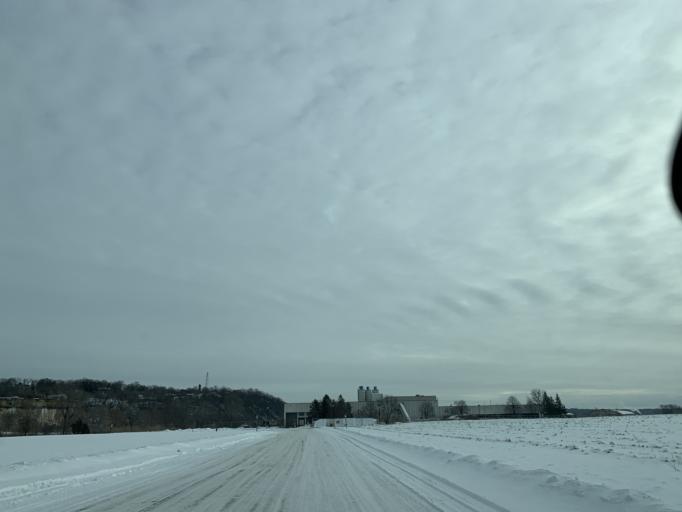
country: US
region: Minnesota
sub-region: Ramsey County
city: Saint Paul
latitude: 44.9443
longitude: -93.0698
